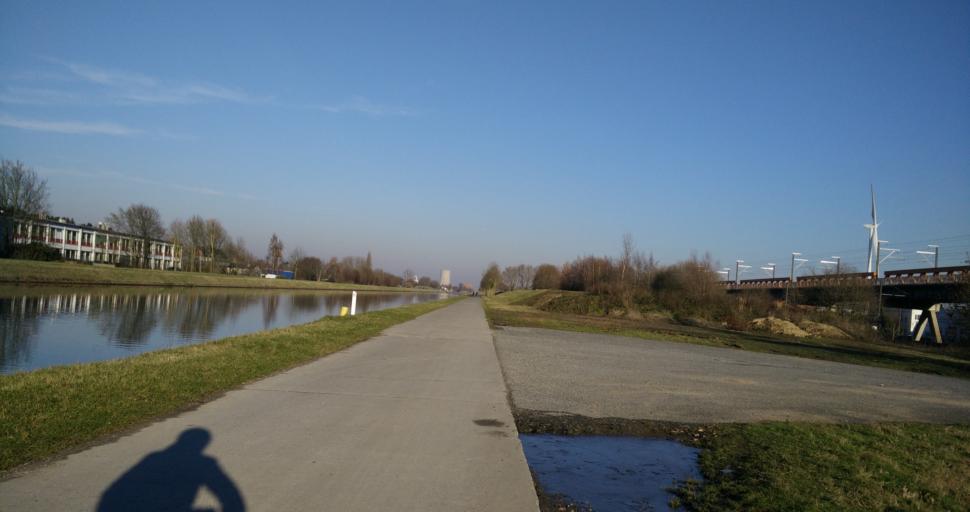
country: BE
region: Flanders
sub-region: Provincie Vlaams-Brabant
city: Beersel
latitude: 50.7697
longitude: 4.2762
